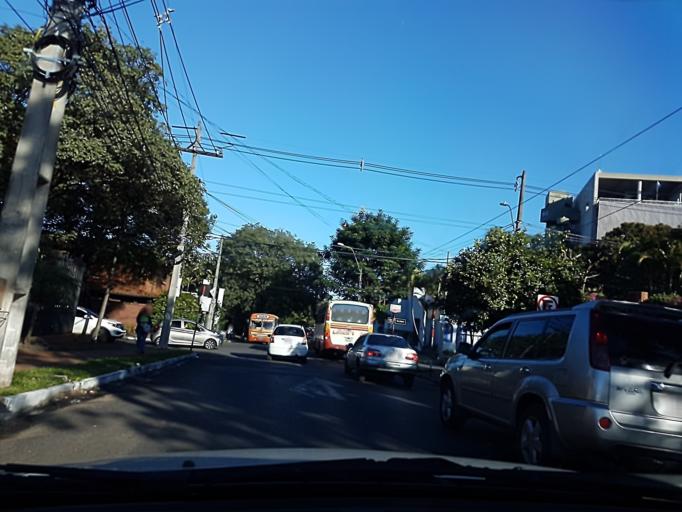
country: PY
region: Asuncion
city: Asuncion
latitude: -25.2795
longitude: -57.5736
